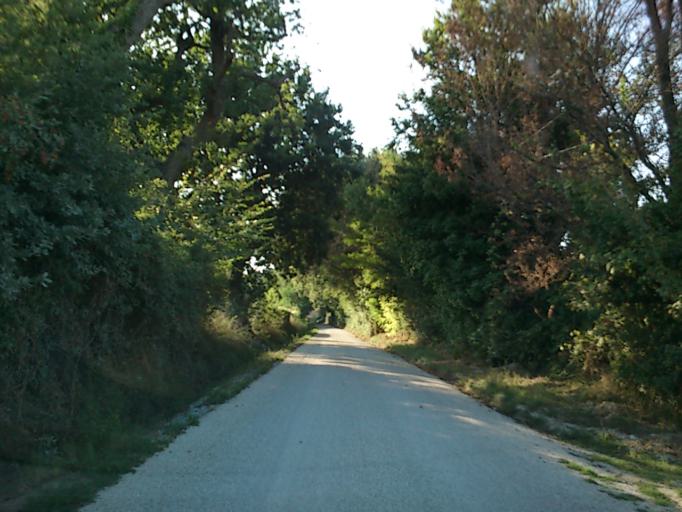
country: IT
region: The Marches
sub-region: Provincia di Pesaro e Urbino
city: Calcinelli
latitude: 43.7610
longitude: 12.9195
